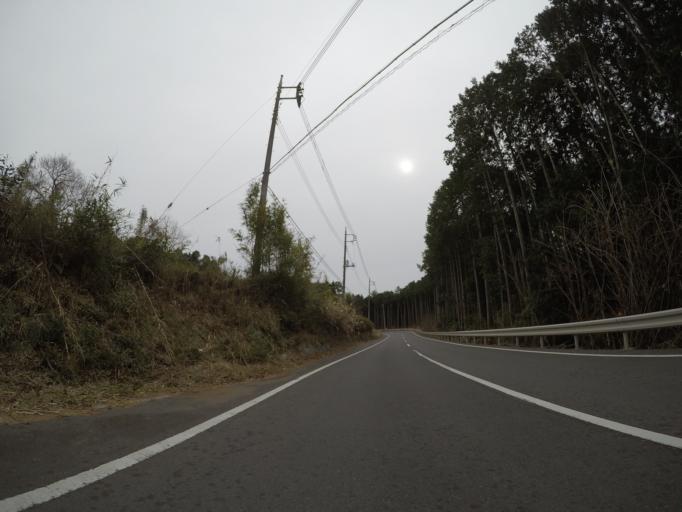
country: JP
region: Shizuoka
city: Fujinomiya
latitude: 35.2387
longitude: 138.5750
